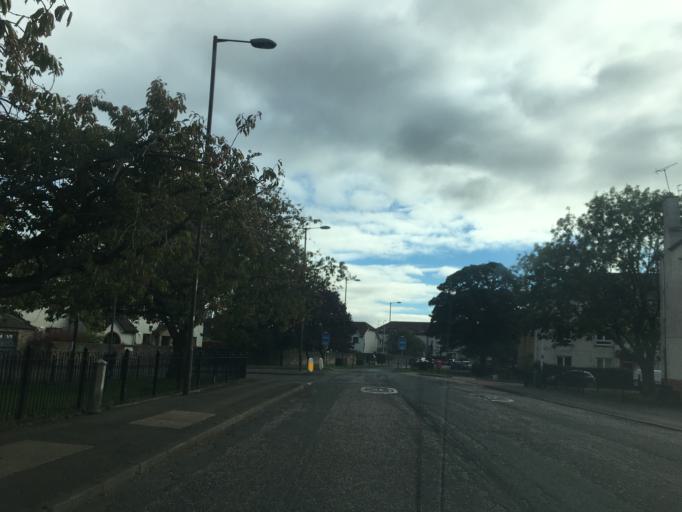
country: GB
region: Scotland
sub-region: West Lothian
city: Seafield
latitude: 55.9328
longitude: -3.1571
